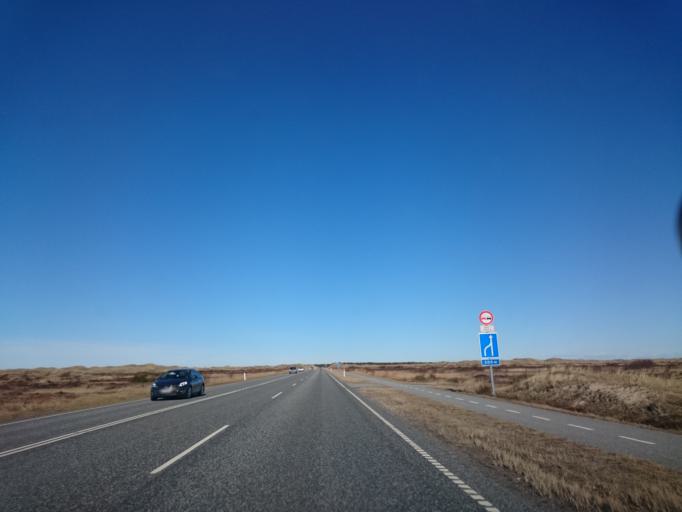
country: DK
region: North Denmark
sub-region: Frederikshavn Kommune
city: Skagen
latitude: 57.6839
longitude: 10.4657
